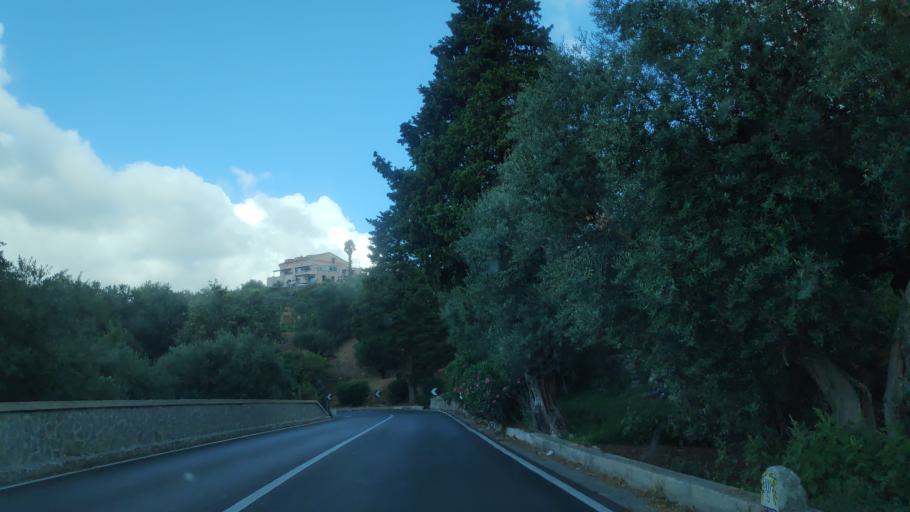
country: IT
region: Campania
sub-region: Provincia di Napoli
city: Arola-Preazzano
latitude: 40.6166
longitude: 14.4349
